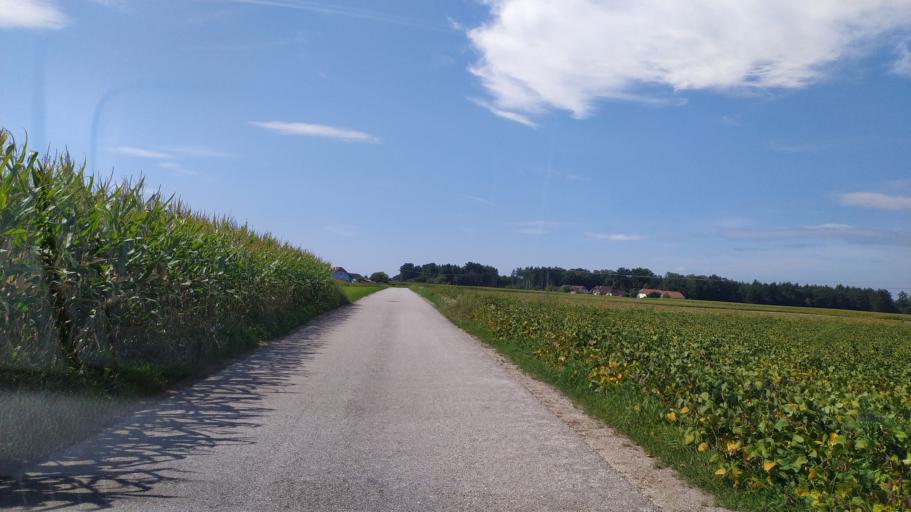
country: AT
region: Upper Austria
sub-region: Politischer Bezirk Perg
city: Perg
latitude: 48.2002
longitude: 14.6879
